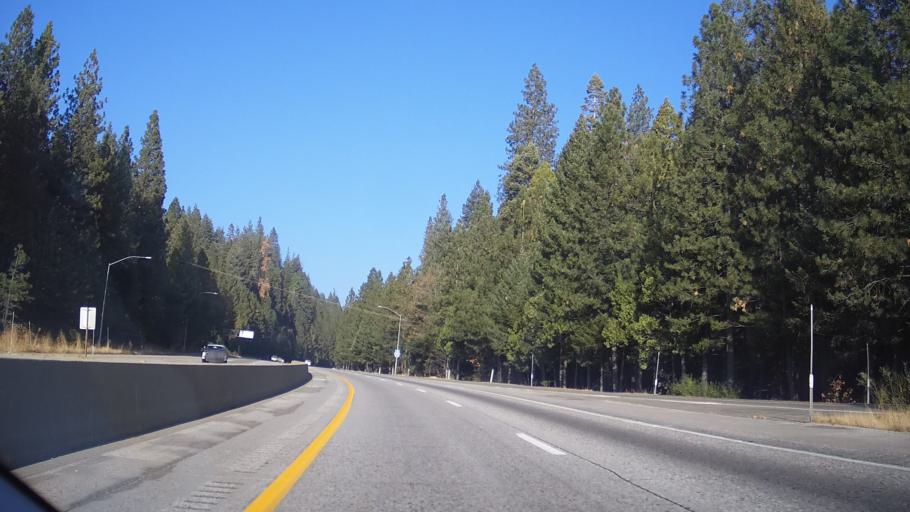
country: US
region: California
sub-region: Placer County
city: Foresthill
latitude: 39.2155
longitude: -120.7759
